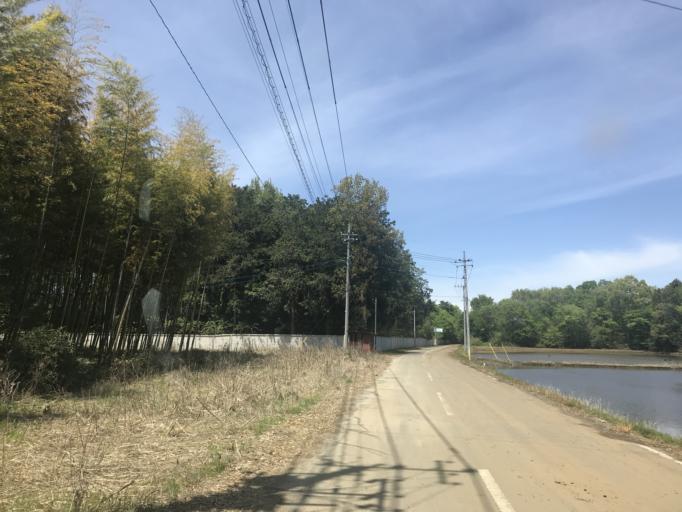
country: JP
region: Ibaraki
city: Shimodate
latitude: 36.2849
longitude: 140.0213
